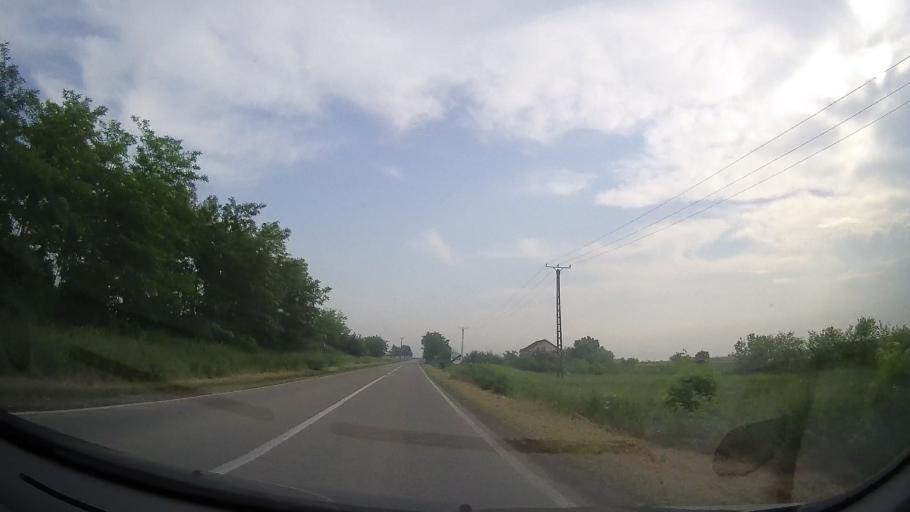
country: RO
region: Timis
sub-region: Comuna Sag
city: Sag
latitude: 45.6601
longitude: 21.1490
